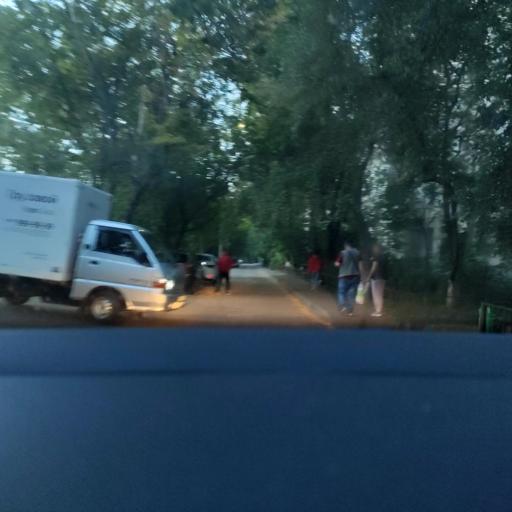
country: RU
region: Moskovskaya
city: Reutov
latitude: 55.7682
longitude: 37.8566
